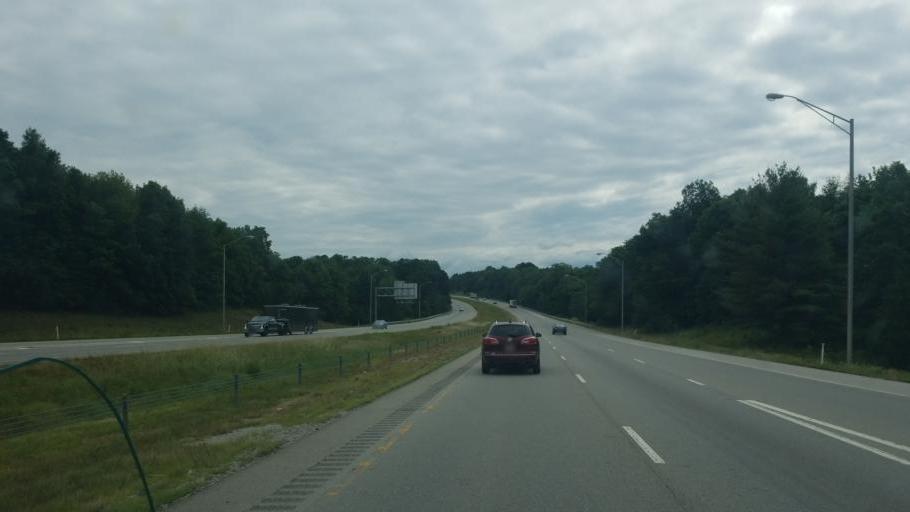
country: US
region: Indiana
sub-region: Putnam County
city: Cloverdale
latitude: 39.5326
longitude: -86.7979
